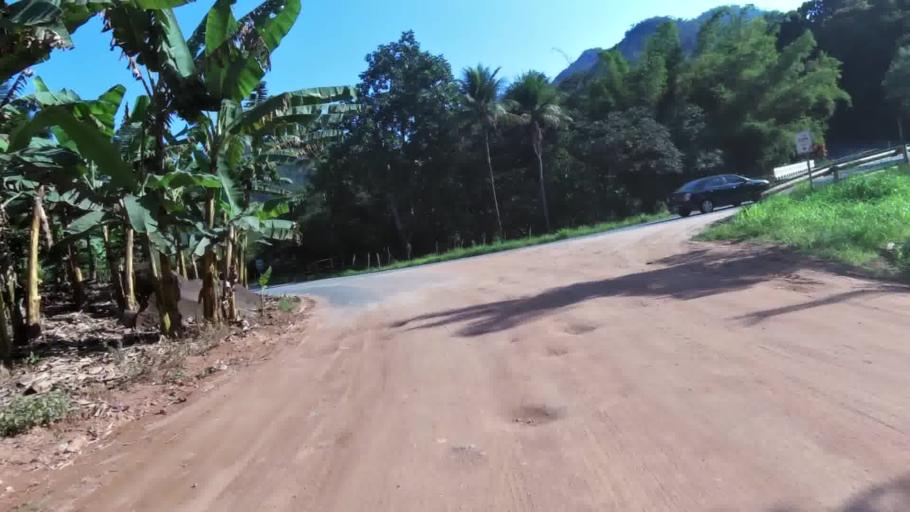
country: BR
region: Espirito Santo
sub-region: Alfredo Chaves
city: Alfredo Chaves
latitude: -20.6138
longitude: -40.7776
